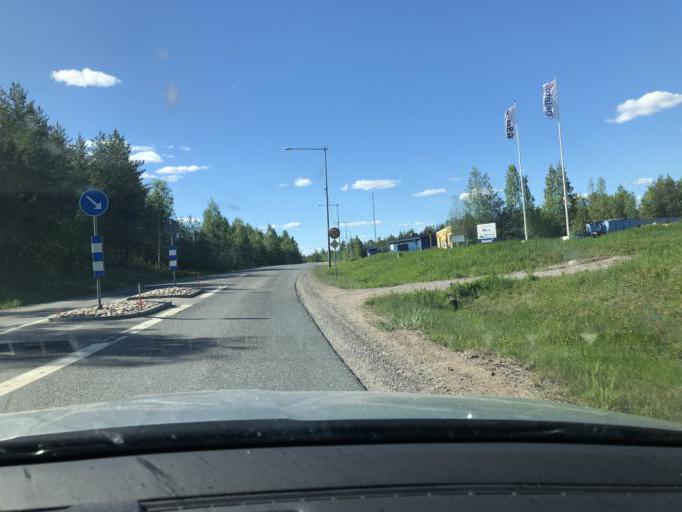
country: SE
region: Norrbotten
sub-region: Kalix Kommun
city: Kalix
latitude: 65.8597
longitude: 23.1602
